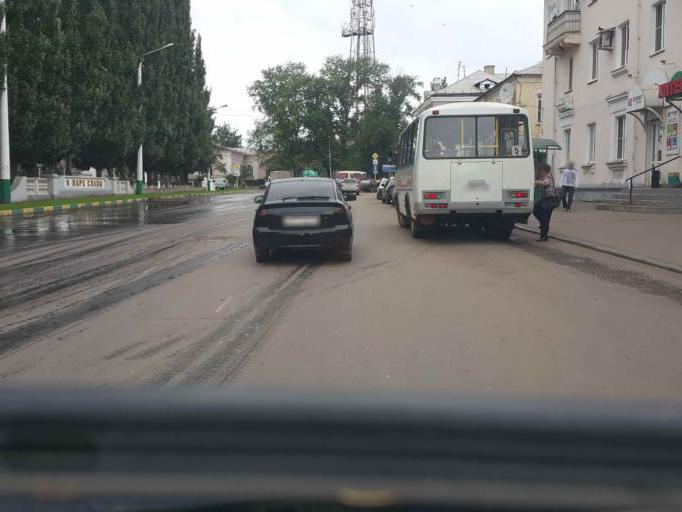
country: RU
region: Tambov
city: Michurinsk
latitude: 52.8940
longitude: 40.4993
